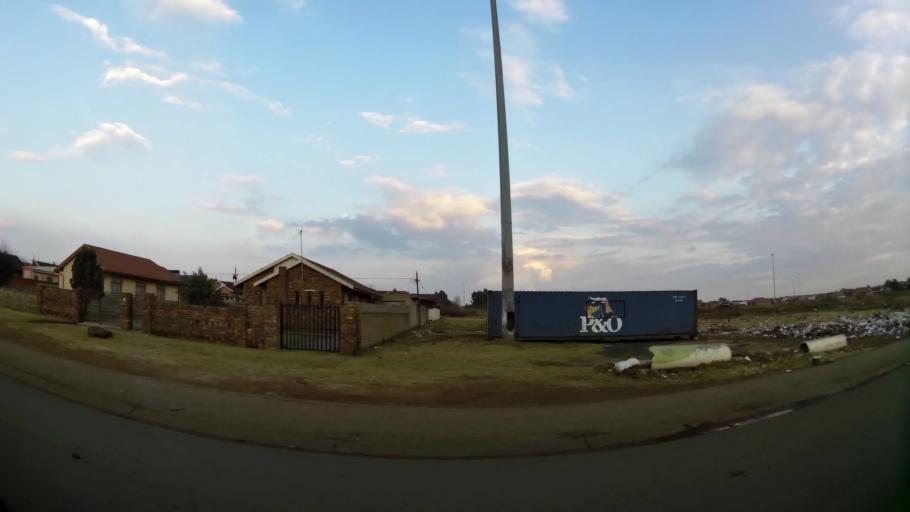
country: ZA
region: Gauteng
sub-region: City of Johannesburg Metropolitan Municipality
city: Orange Farm
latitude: -26.5631
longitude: 27.8519
